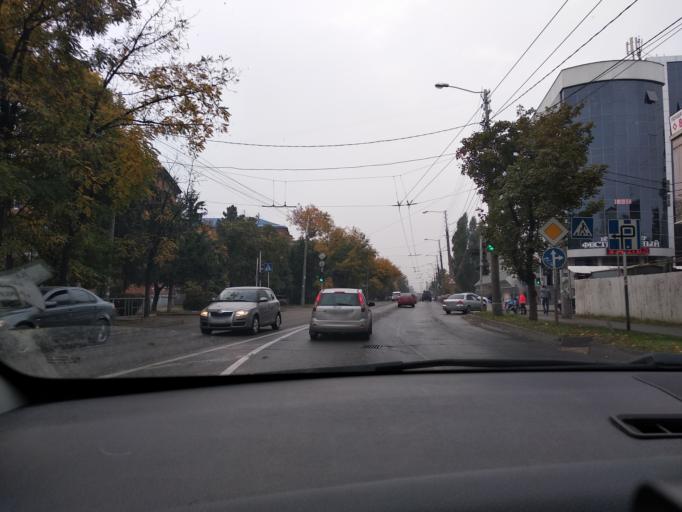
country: RU
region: Krasnodarskiy
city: Krasnodar
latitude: 45.0568
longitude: 38.9608
